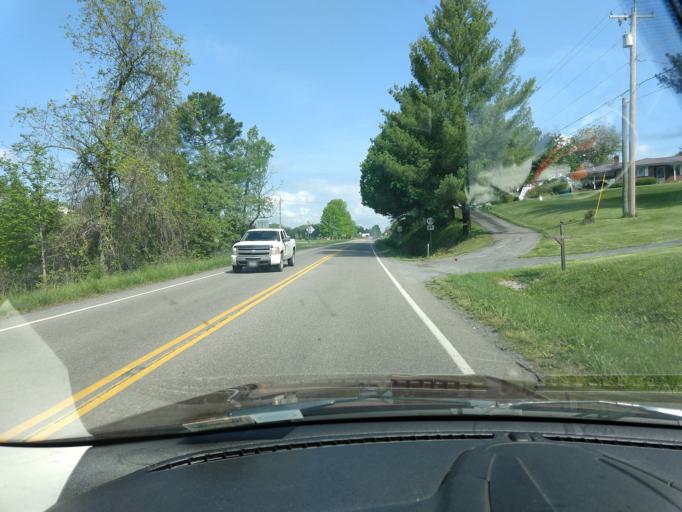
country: US
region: Virginia
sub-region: Russell County
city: Honaker
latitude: 36.9614
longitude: -81.9334
